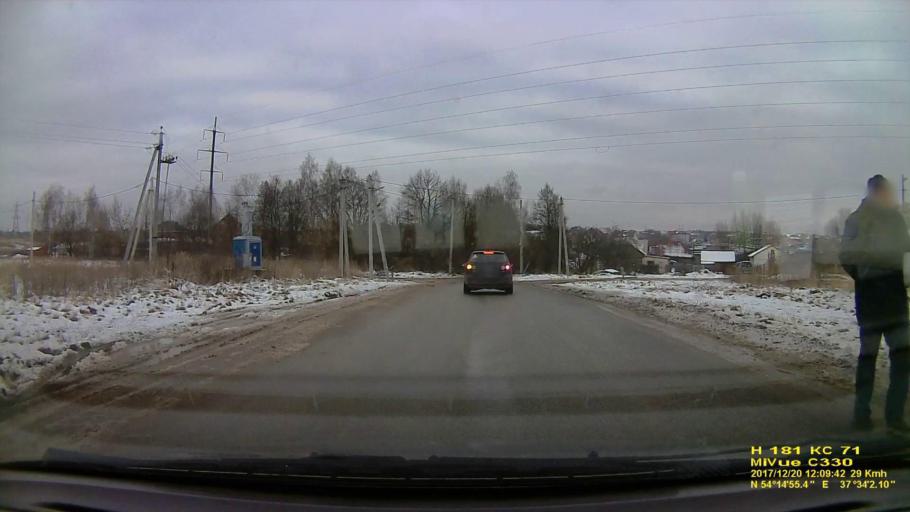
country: RU
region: Tula
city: Gorelki
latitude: 54.2488
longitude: 37.5673
